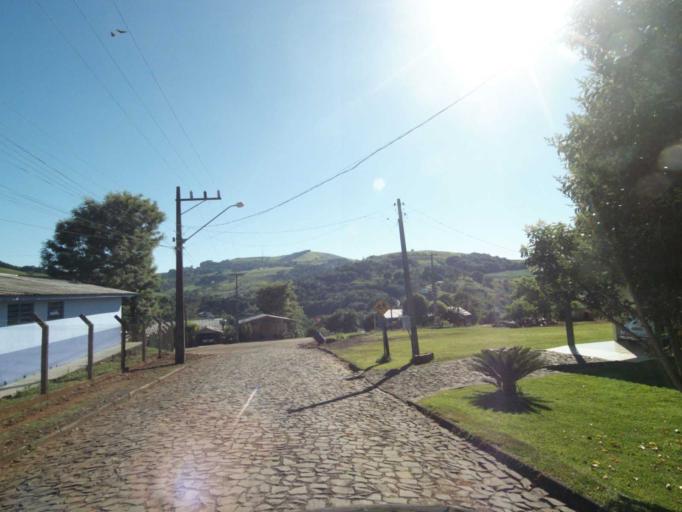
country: BR
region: Parana
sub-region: Francisco Beltrao
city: Francisco Beltrao
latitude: -26.1452
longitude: -53.3095
